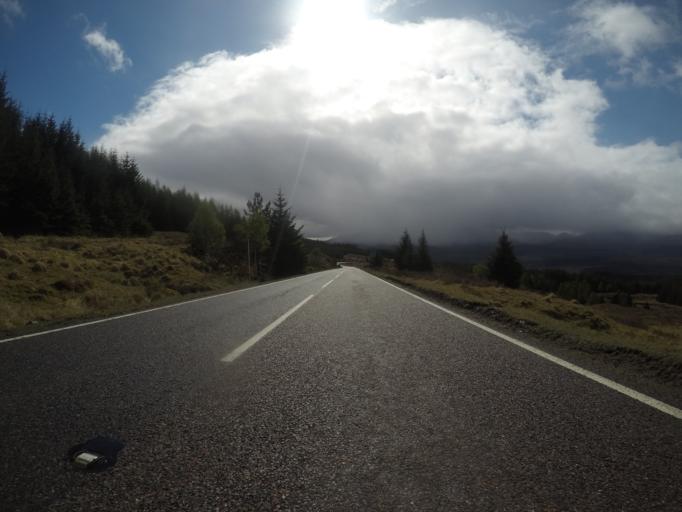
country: GB
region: Scotland
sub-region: Highland
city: Spean Bridge
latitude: 57.0917
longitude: -4.9851
